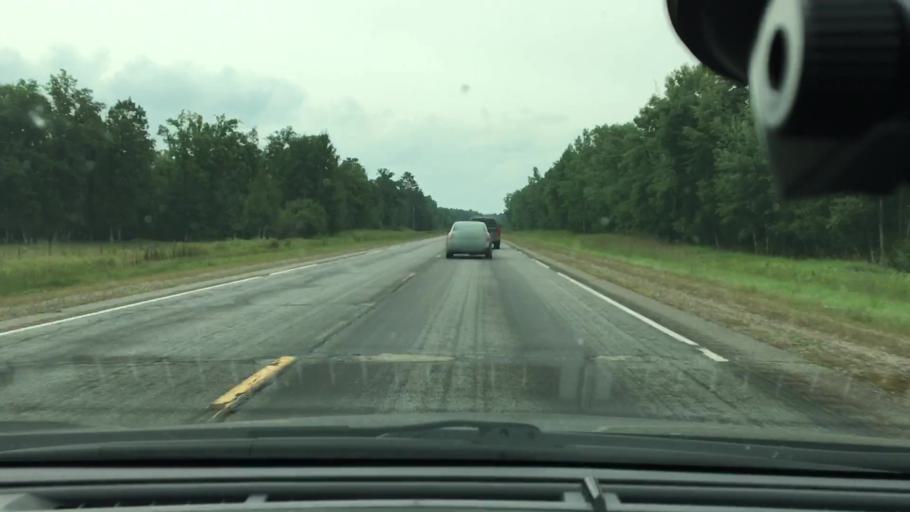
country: US
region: Minnesota
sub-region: Crow Wing County
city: Cross Lake
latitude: 46.6776
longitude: -93.9526
